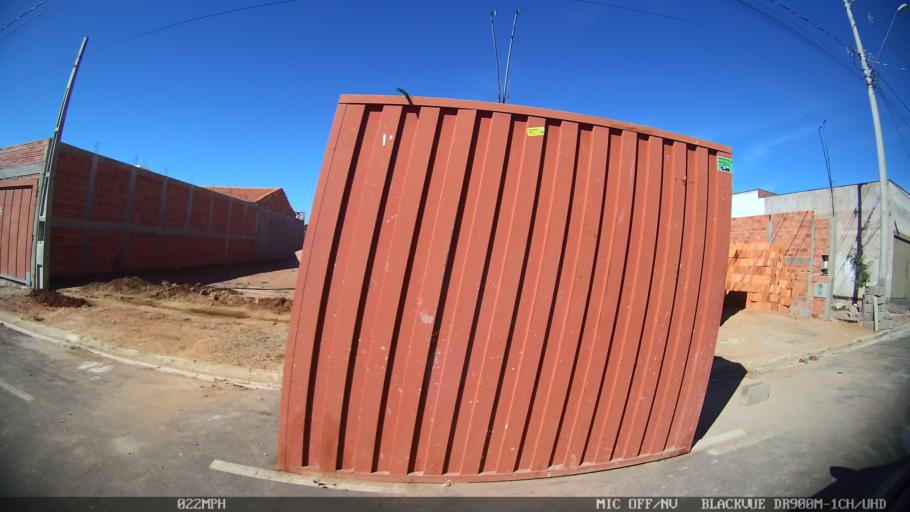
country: BR
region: Sao Paulo
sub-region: Franca
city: Franca
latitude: -20.5676
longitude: -47.3463
